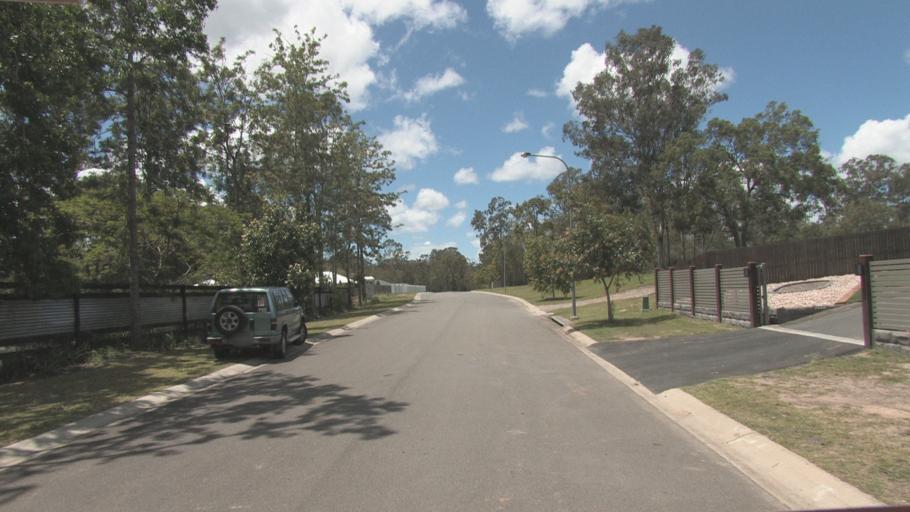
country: AU
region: Queensland
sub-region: Logan
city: Beenleigh
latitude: -27.6660
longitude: 153.2189
